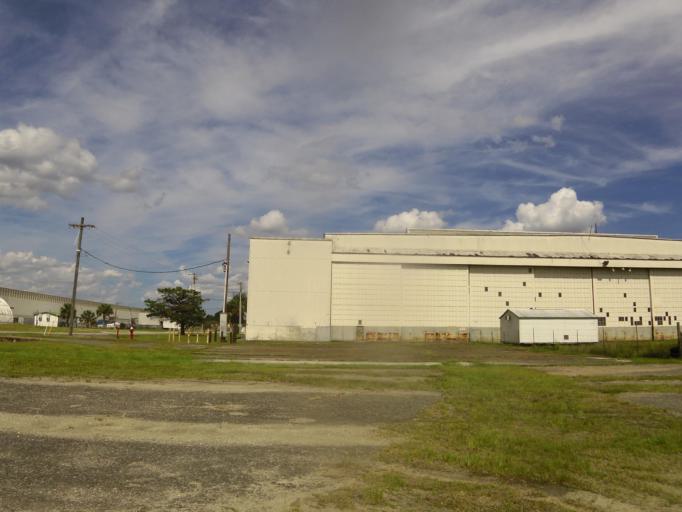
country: US
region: Florida
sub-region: Clay County
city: Green Cove Springs
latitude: 29.9766
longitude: -81.6603
